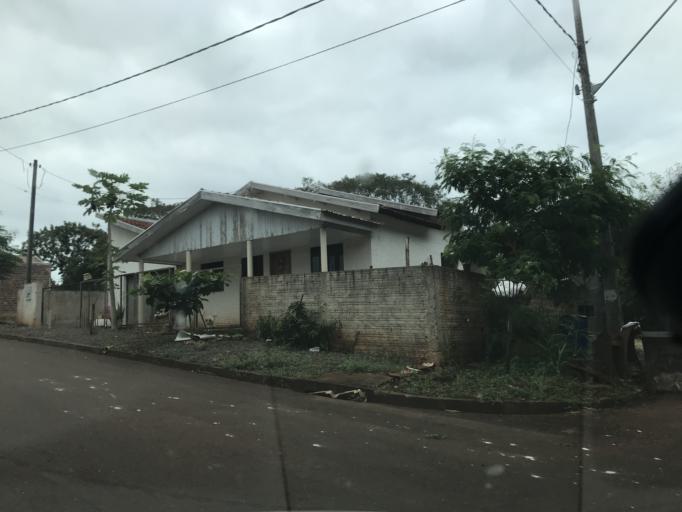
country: BR
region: Parana
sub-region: Palotina
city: Palotina
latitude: -24.2990
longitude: -53.8275
